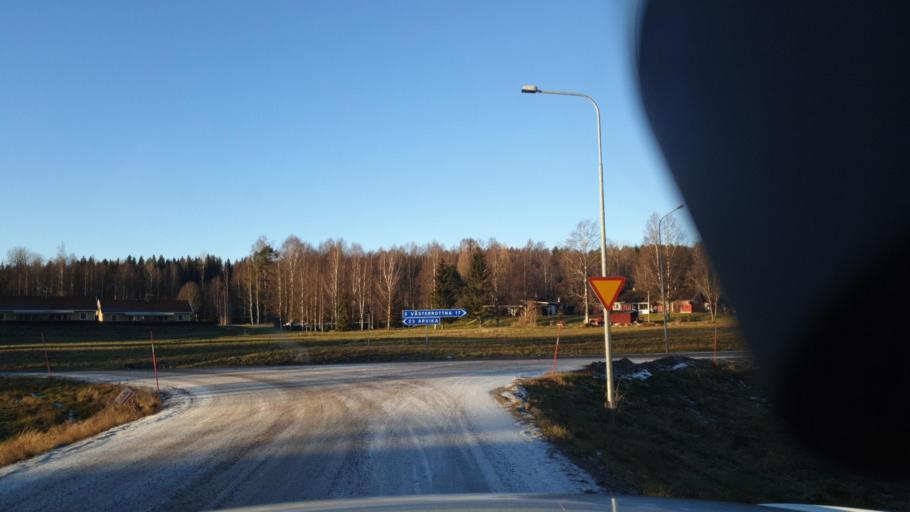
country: SE
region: Vaermland
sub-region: Arvika Kommun
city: Arvika
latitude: 59.7510
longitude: 12.8232
